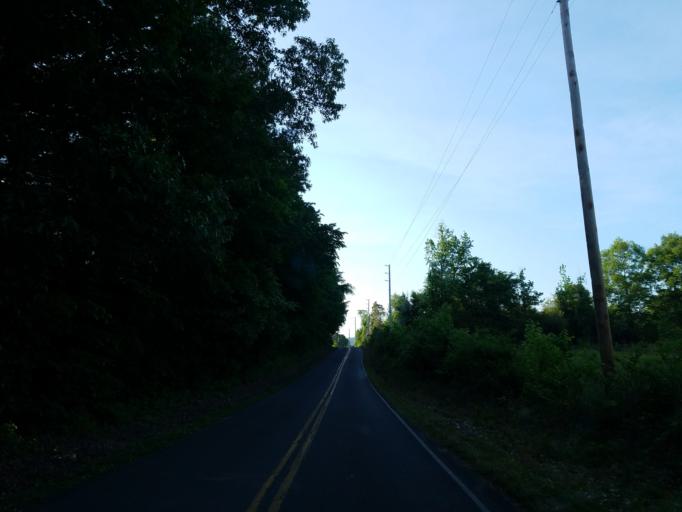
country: US
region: Georgia
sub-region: Gordon County
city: Calhoun
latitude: 34.5019
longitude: -85.1155
